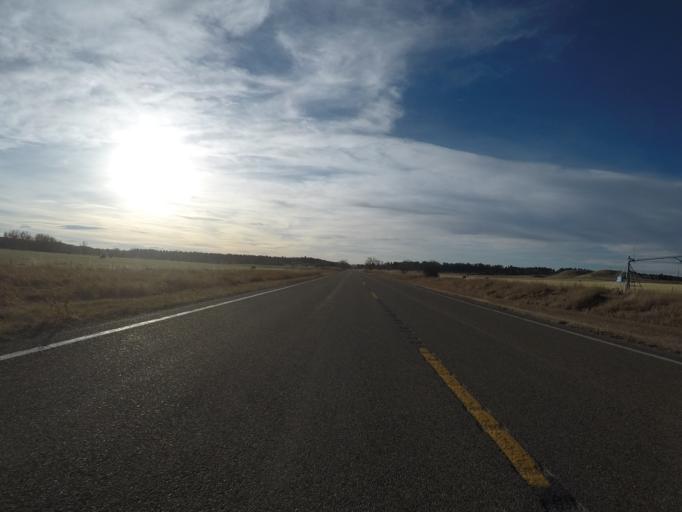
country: US
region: Montana
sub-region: Musselshell County
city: Roundup
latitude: 46.3415
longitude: -108.6876
